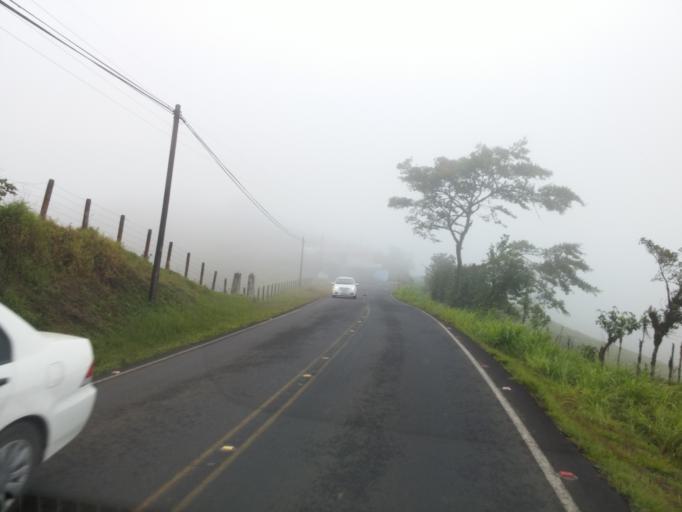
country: CR
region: Alajuela
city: San Ramon
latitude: 10.1578
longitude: -84.4955
